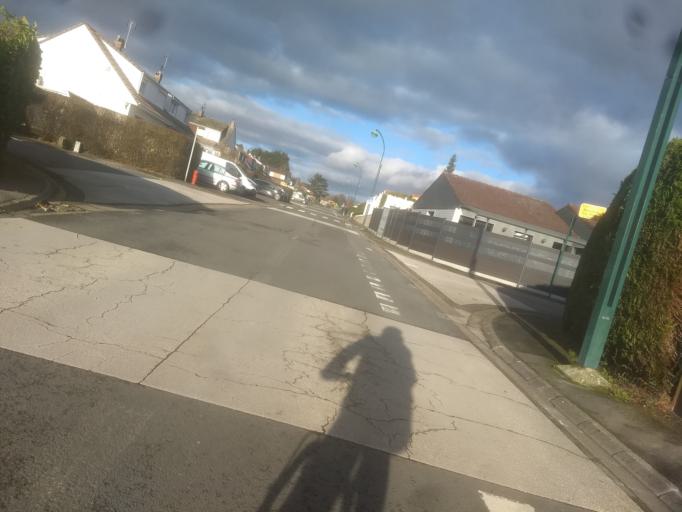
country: FR
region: Nord-Pas-de-Calais
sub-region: Departement du Pas-de-Calais
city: Saint-Laurent-Blangy
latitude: 50.3028
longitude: 2.8002
